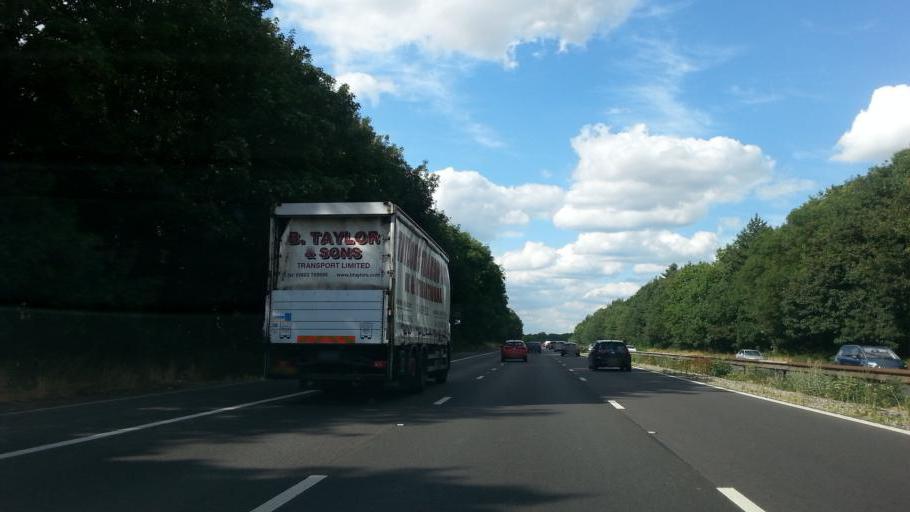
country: GB
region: England
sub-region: Leicestershire
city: Lutterworth
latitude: 52.4943
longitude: -1.1910
